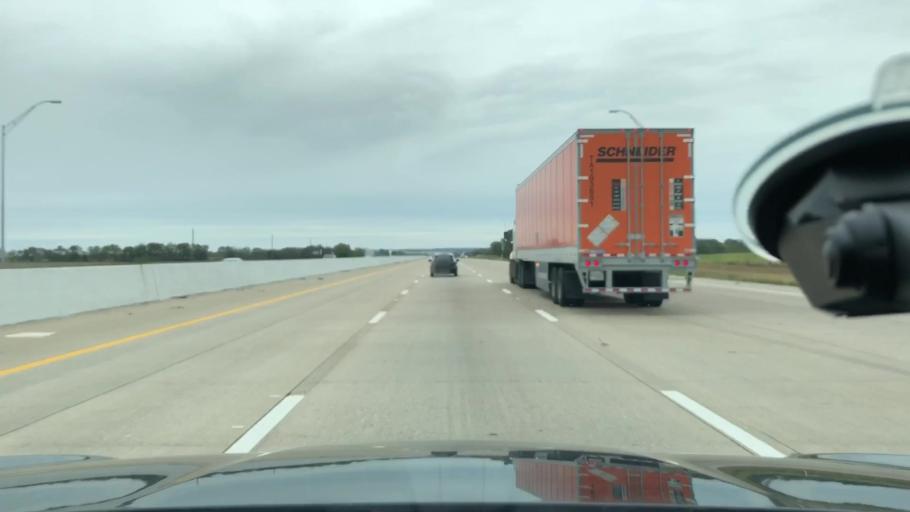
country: US
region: Texas
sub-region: Ellis County
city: Italy
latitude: 32.2026
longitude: -96.8960
